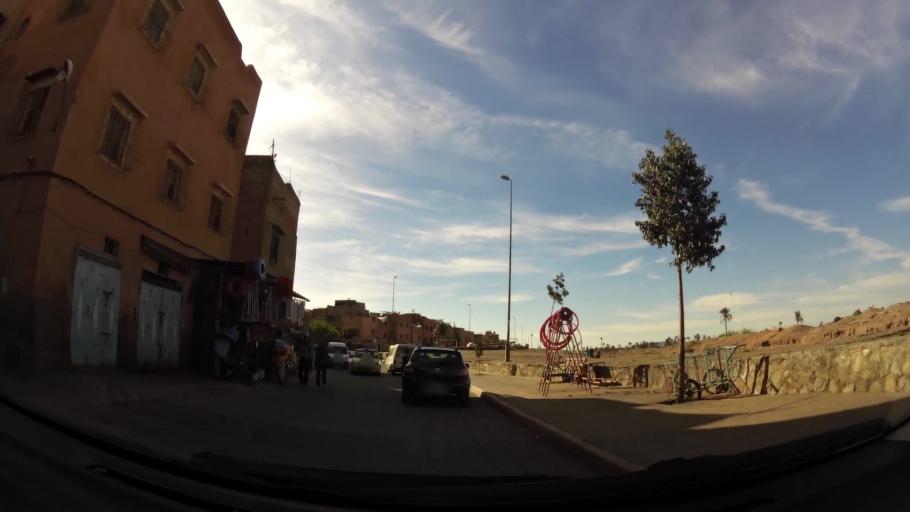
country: MA
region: Marrakech-Tensift-Al Haouz
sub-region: Marrakech
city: Marrakesh
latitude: 31.6168
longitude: -7.9638
